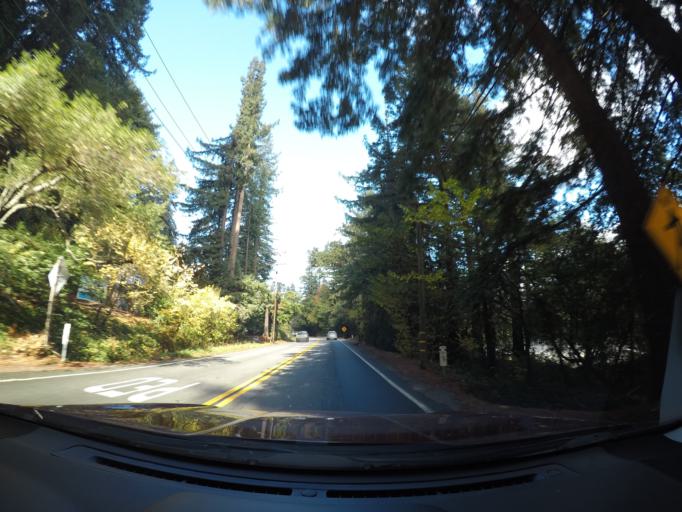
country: US
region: California
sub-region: Santa Cruz County
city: Ben Lomond
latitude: 37.0803
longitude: -122.0839
